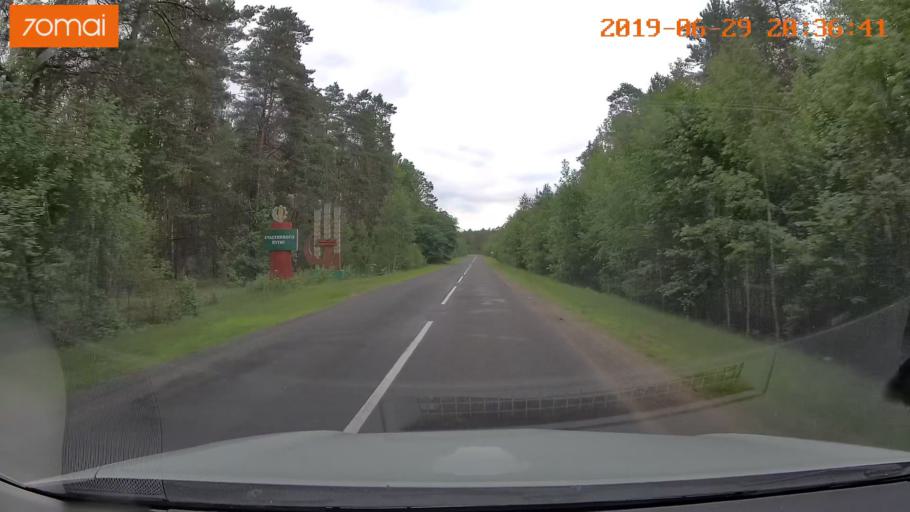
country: BY
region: Brest
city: Hantsavichy
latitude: 52.5289
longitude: 26.3604
